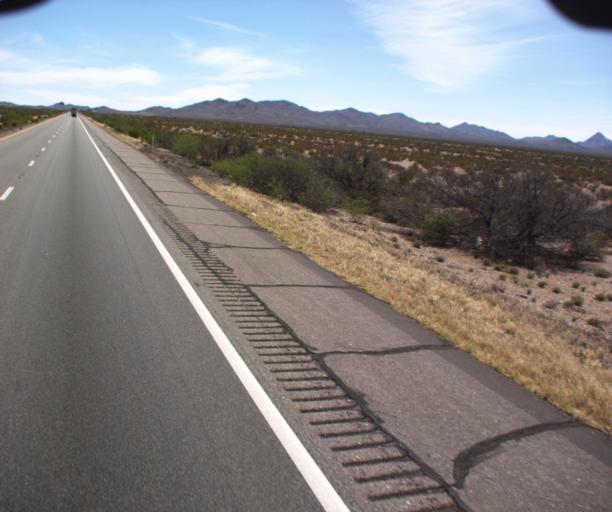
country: US
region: New Mexico
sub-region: Hidalgo County
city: Lordsburg
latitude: 32.2334
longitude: -109.0747
